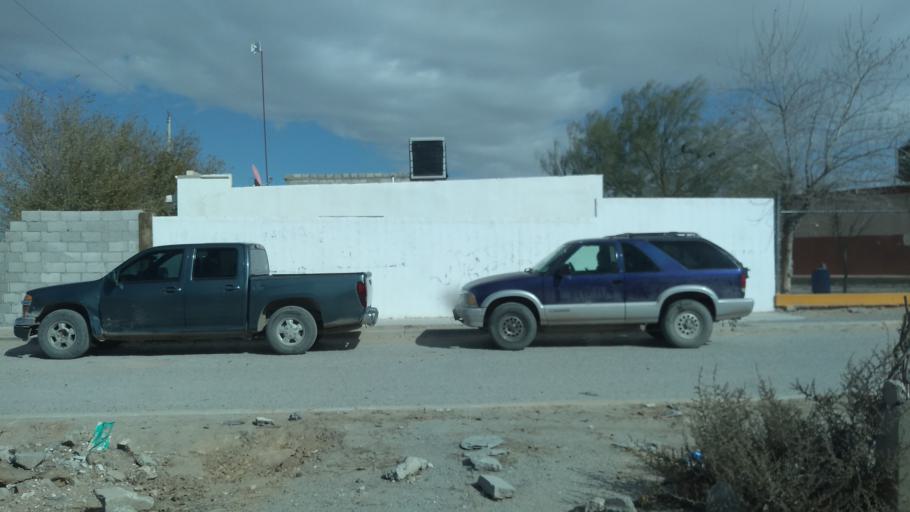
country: US
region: Texas
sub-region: El Paso County
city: San Elizario
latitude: 31.5769
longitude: -106.3452
